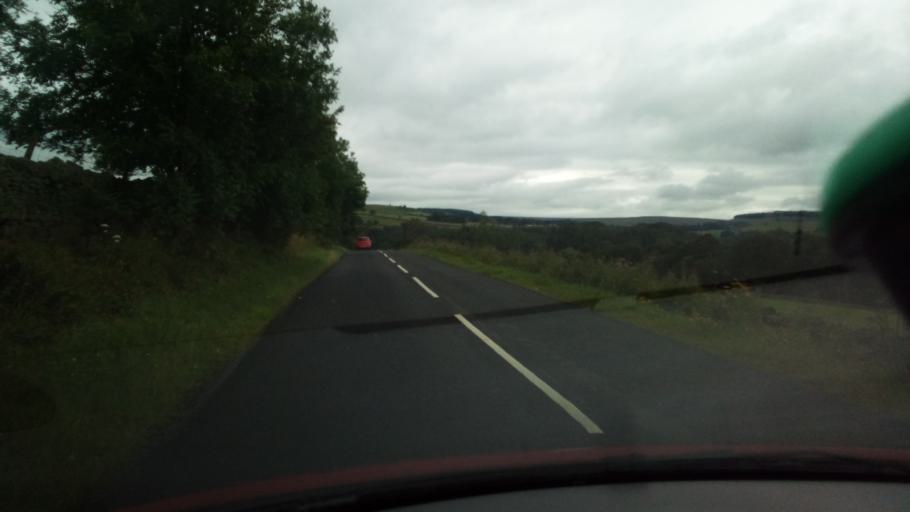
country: GB
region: England
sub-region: Northumberland
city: Slaley
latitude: 54.8511
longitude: -2.0324
